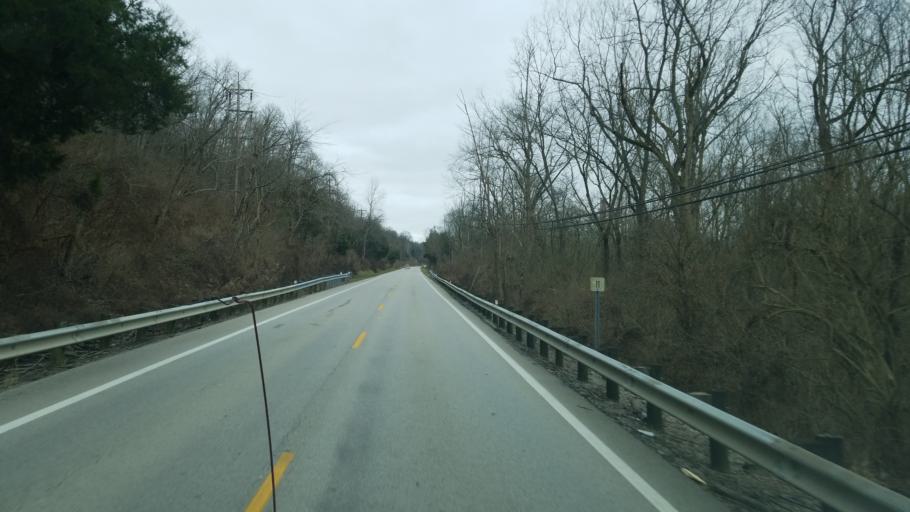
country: US
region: Ohio
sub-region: Clermont County
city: New Richmond
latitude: 38.8854
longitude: -84.2290
